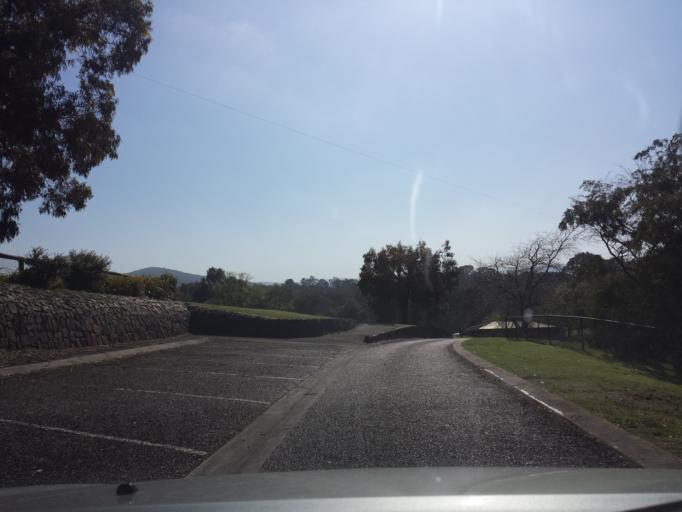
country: AU
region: Victoria
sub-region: Nillumbik
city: Saint Andrews
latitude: -37.6617
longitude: 145.2911
